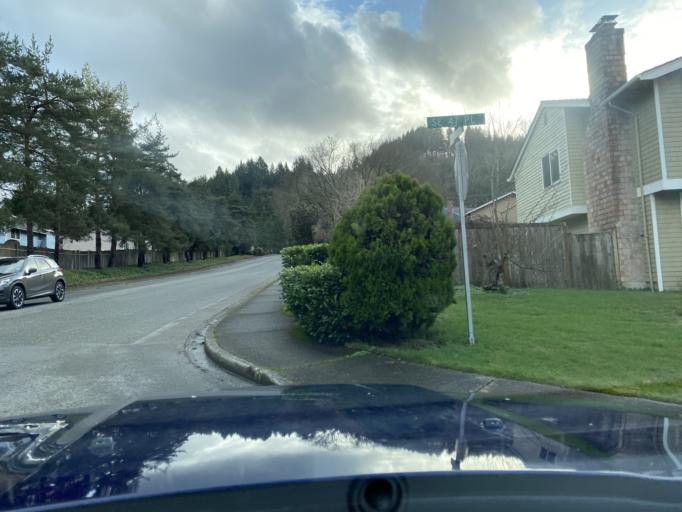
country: US
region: Washington
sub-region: King County
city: West Lake Sammamish
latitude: 47.5599
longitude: -122.0848
